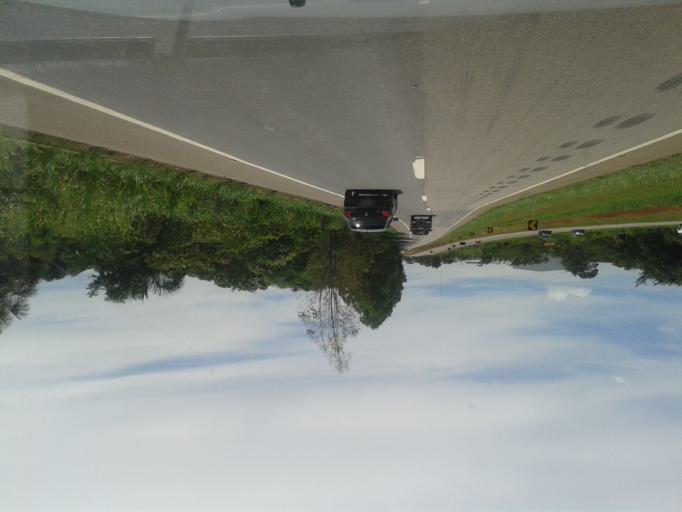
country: BR
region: Goias
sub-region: Hidrolandia
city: Hidrolandia
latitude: -17.0196
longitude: -49.2213
